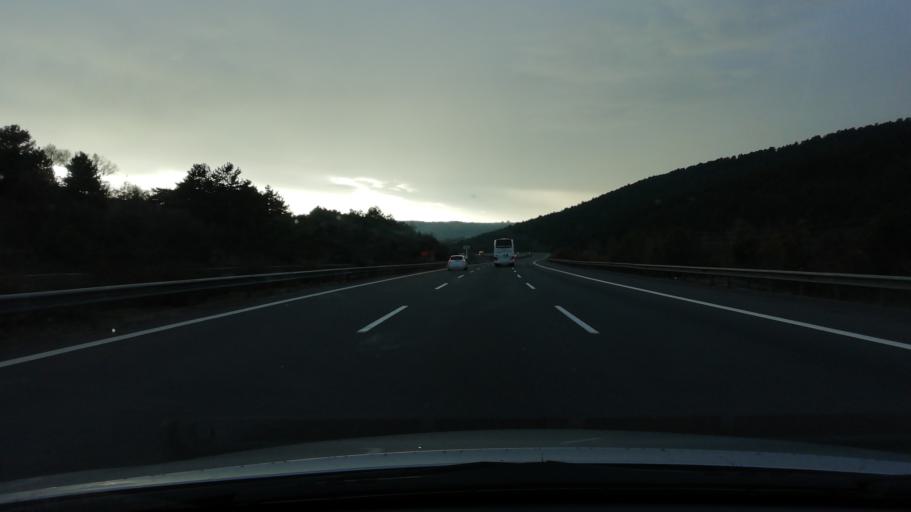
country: TR
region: Bolu
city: Gokcesu
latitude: 40.7394
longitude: 31.8338
